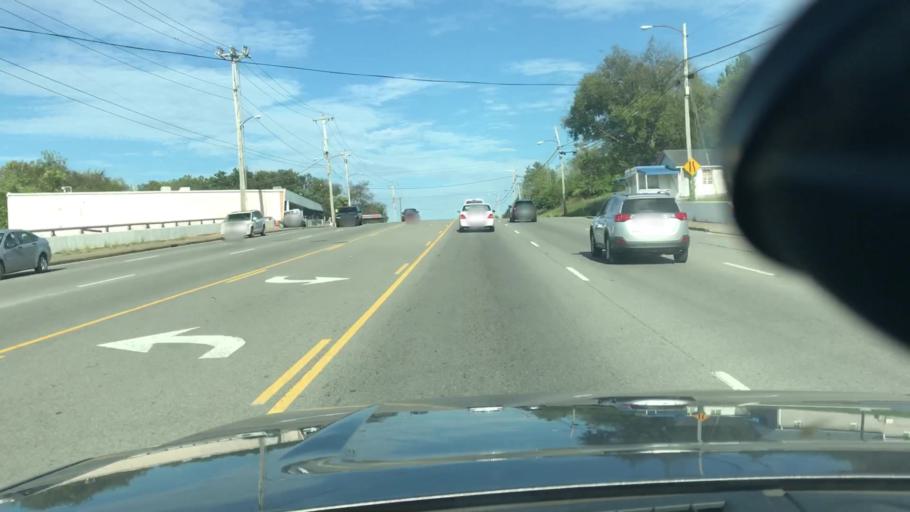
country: US
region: Tennessee
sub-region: Davidson County
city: Nashville
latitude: 36.1944
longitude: -86.8324
